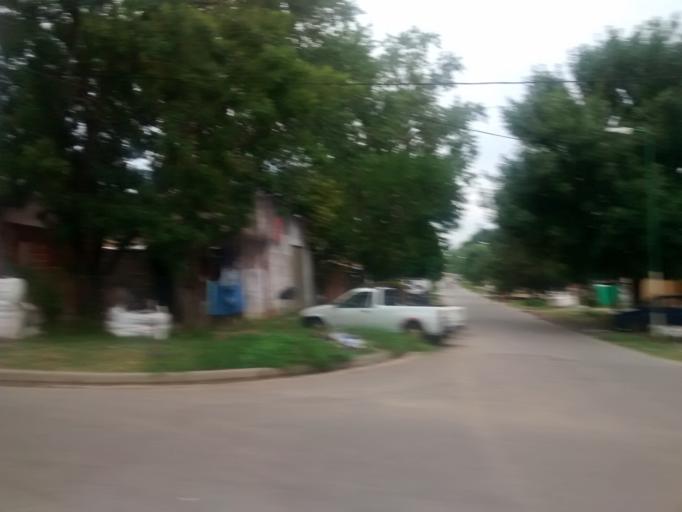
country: AR
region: Buenos Aires
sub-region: Partido de La Plata
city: La Plata
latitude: -34.9448
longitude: -57.9323
